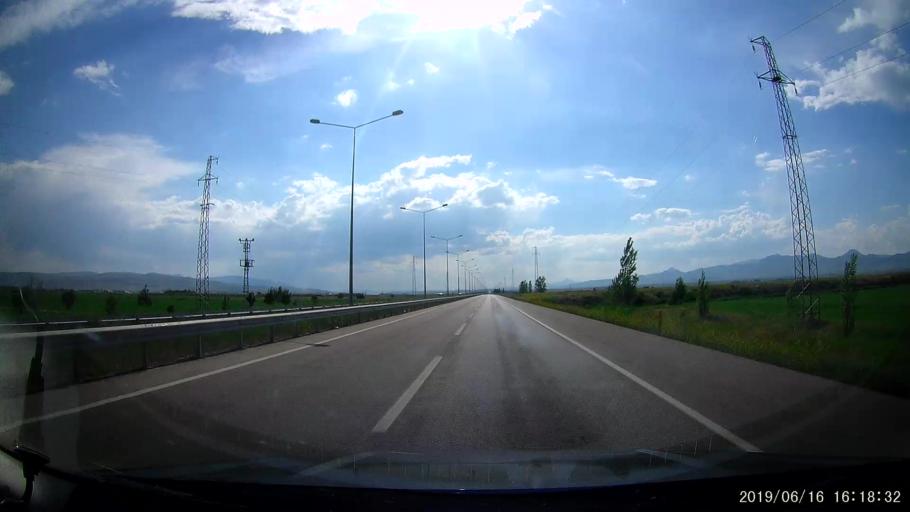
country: TR
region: Erzurum
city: Ilica
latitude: 39.9651
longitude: 41.1663
